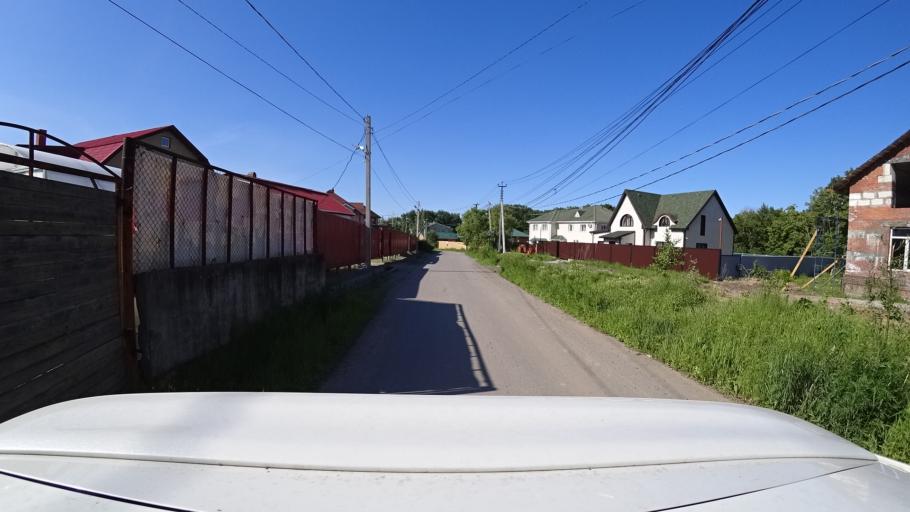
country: RU
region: Khabarovsk Krai
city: Topolevo
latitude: 48.5418
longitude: 135.1791
